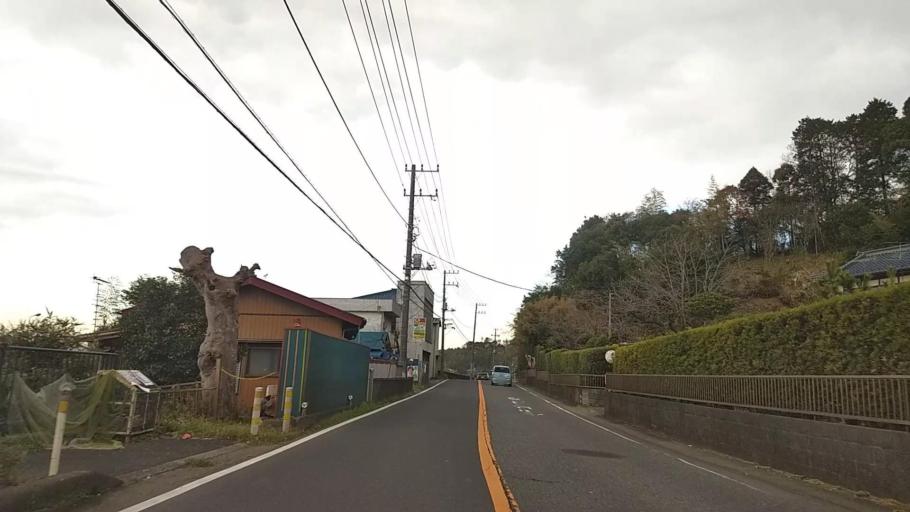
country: JP
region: Chiba
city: Yotsukaido
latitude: 35.6052
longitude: 140.1954
